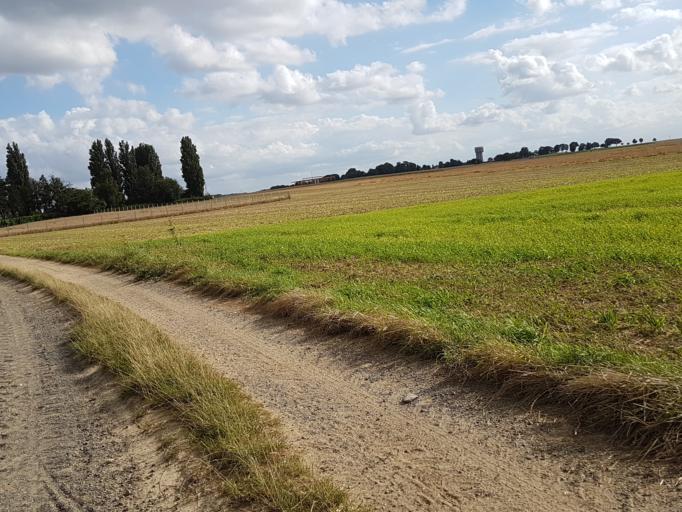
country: BE
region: Flanders
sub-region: Provincie Vlaams-Brabant
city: Kortenberg
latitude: 50.9067
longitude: 4.5392
